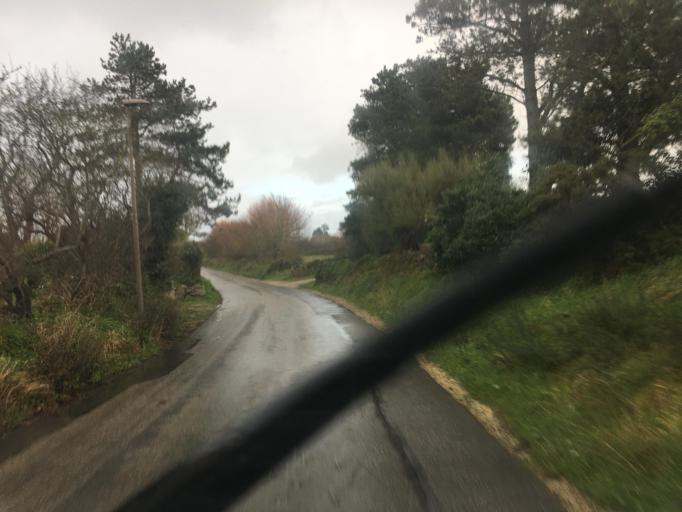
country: FR
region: Lower Normandy
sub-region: Departement de la Manche
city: Reville
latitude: 49.6887
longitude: -1.2813
